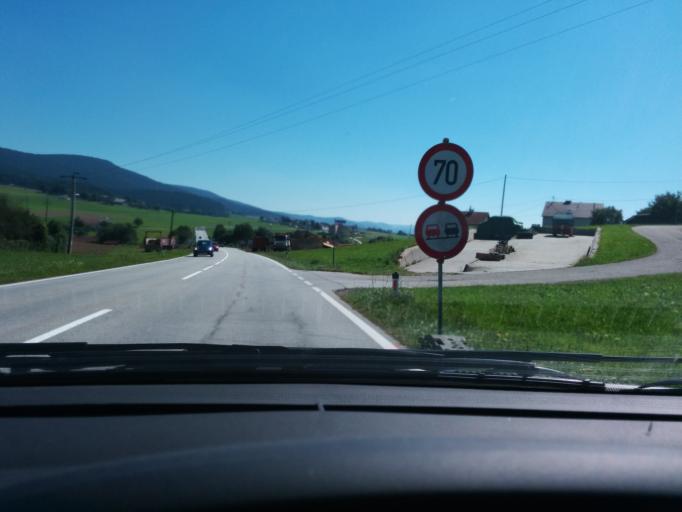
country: AT
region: Upper Austria
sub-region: Politischer Bezirk Rohrbach
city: Ulrichsberg
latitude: 48.6753
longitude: 13.9157
